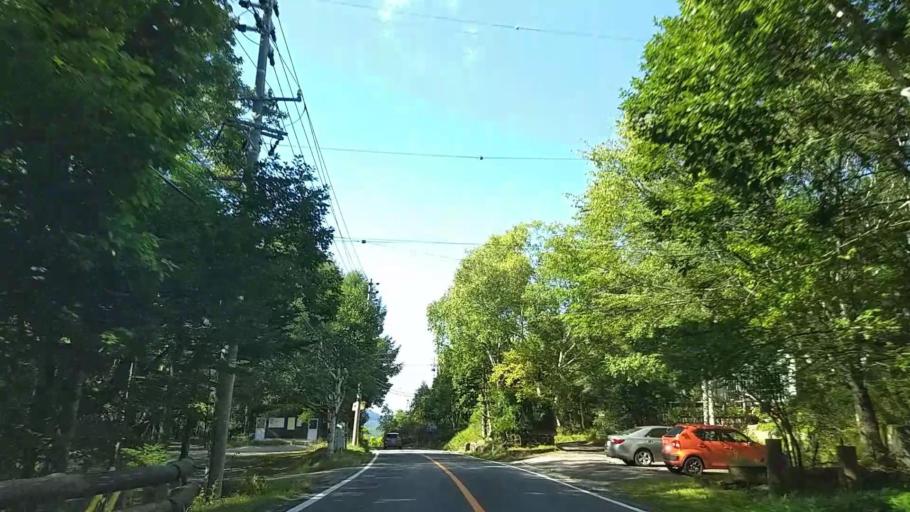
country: JP
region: Nagano
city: Chino
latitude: 36.1053
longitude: 138.2462
